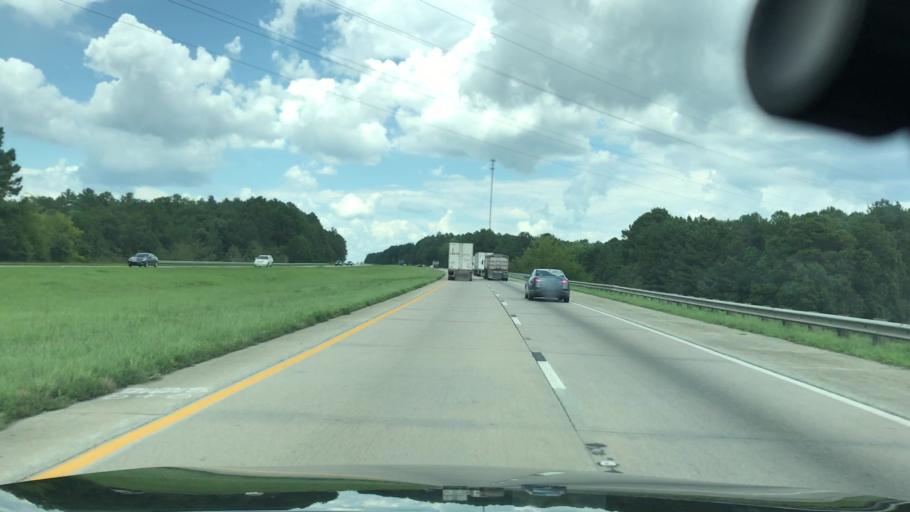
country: US
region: South Carolina
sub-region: Fairfield County
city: Winnsboro
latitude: 34.4505
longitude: -80.9919
